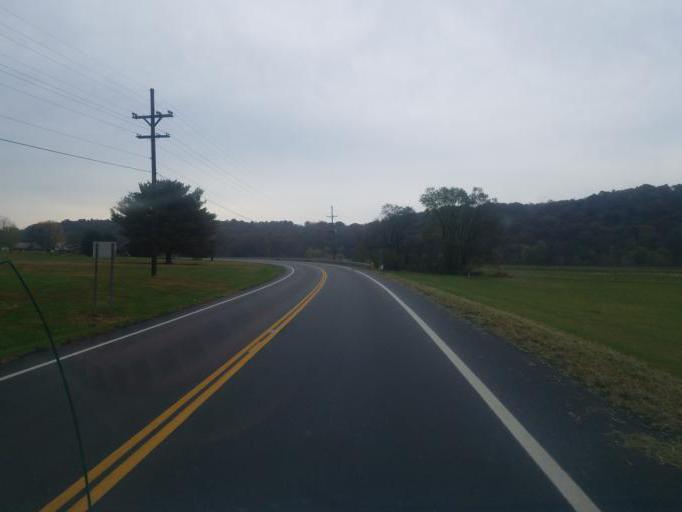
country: US
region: Ohio
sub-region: Washington County
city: Beverly
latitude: 39.5490
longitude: -81.5908
